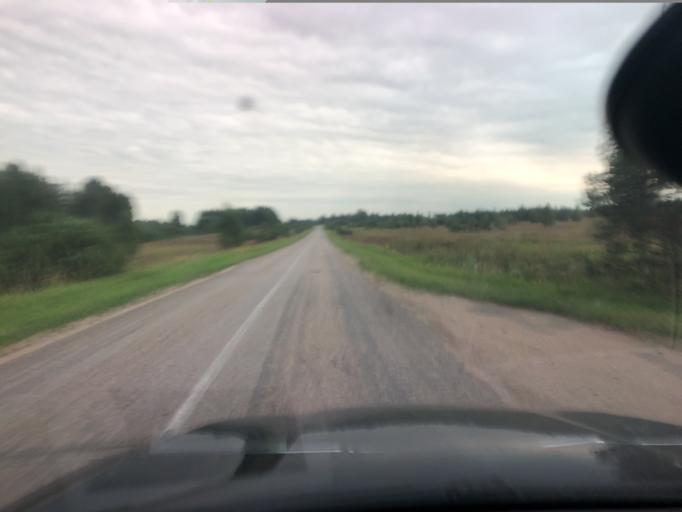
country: RU
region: Jaroslavl
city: Petrovsk
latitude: 57.0019
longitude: 39.0349
